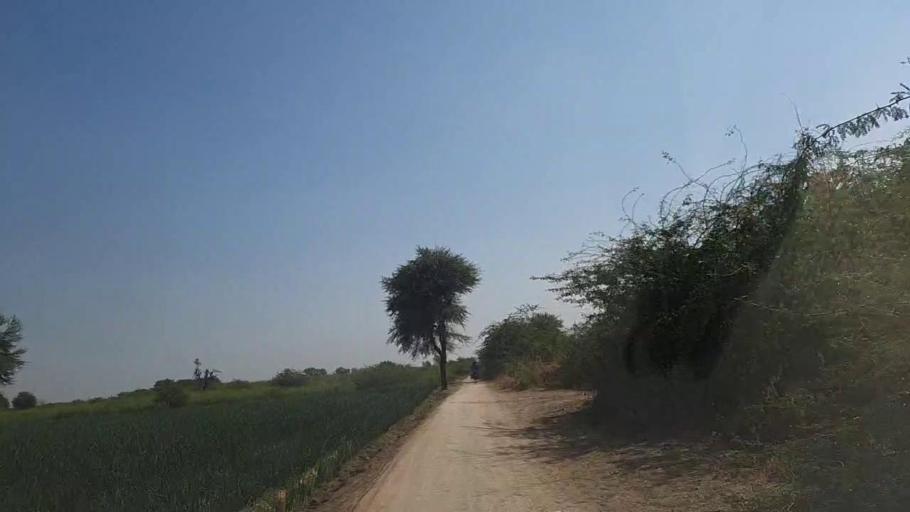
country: PK
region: Sindh
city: Digri
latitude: 25.1662
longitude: 69.1723
